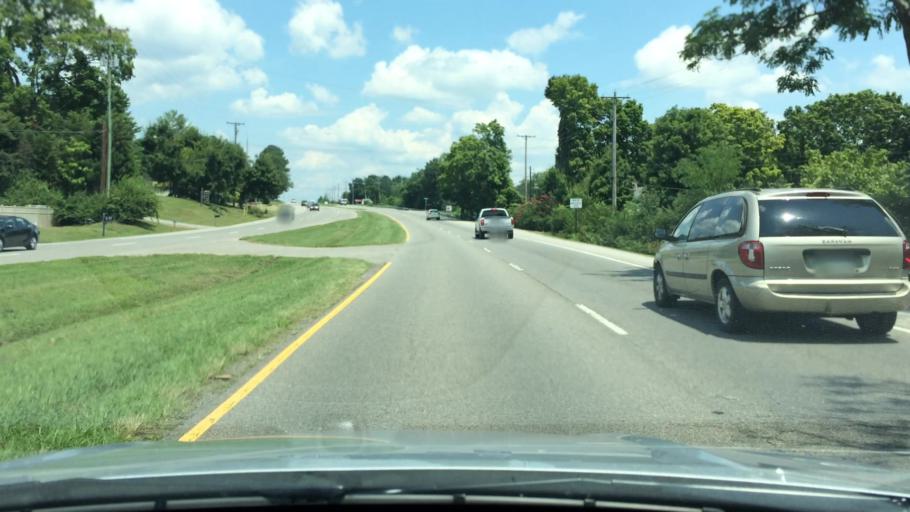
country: US
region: Tennessee
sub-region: Jefferson County
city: Jefferson City
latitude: 36.1685
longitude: -83.4075
